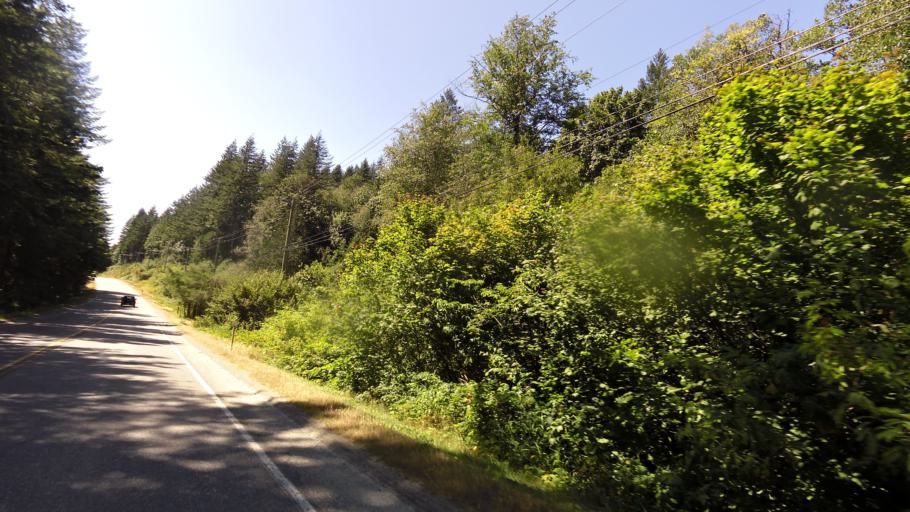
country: CA
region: British Columbia
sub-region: Fraser Valley Regional District
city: Chilliwack
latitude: 49.1993
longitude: -122.0486
